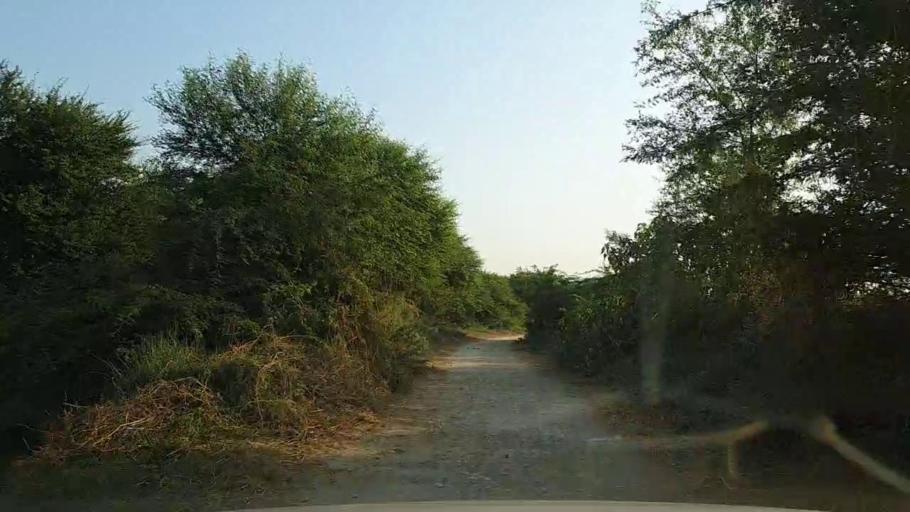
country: PK
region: Sindh
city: Daro Mehar
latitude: 24.7606
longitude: 68.1913
